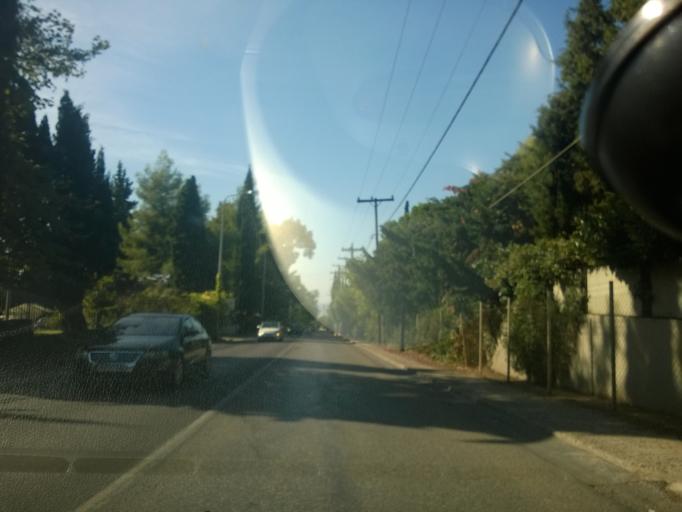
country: GR
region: Central Macedonia
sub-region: Nomos Thessalonikis
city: Pylaia
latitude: 40.5959
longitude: 23.0046
